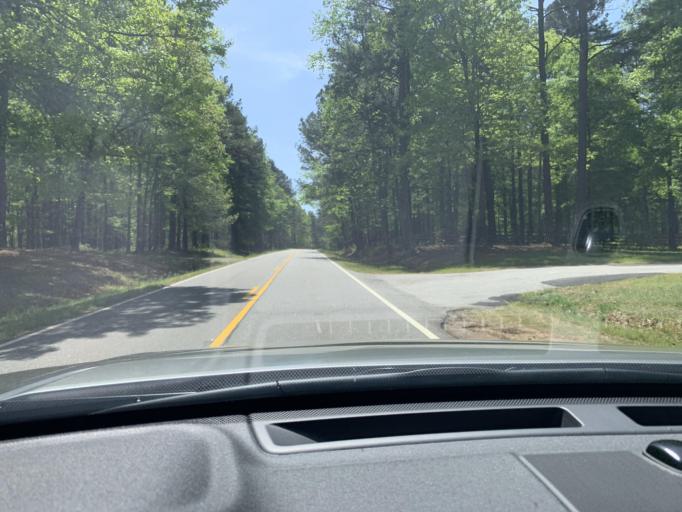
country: US
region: Georgia
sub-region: Oconee County
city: Bogart
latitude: 33.8808
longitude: -83.5558
